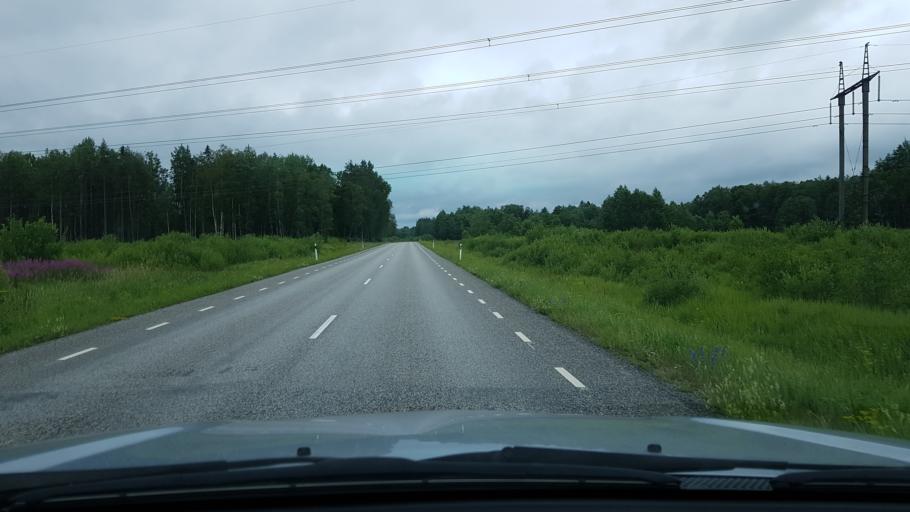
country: EE
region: Ida-Virumaa
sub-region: Narva-Joesuu linn
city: Narva-Joesuu
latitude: 59.3504
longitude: 27.9305
